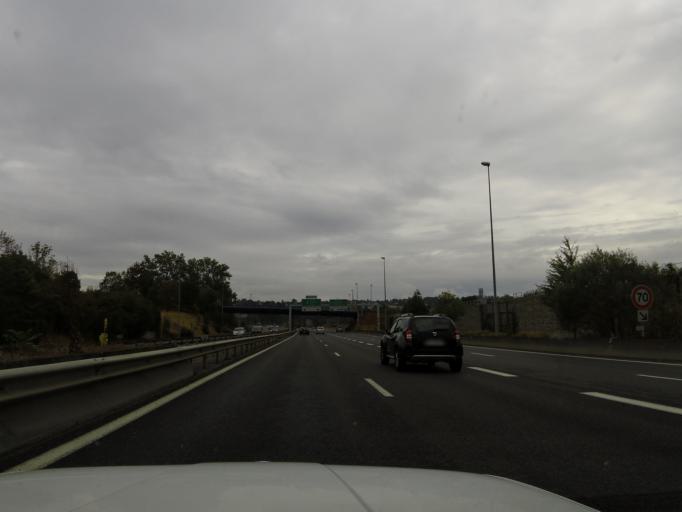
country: FR
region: Rhone-Alpes
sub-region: Departement du Rhone
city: Villeurbanne
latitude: 45.7894
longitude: 4.8856
